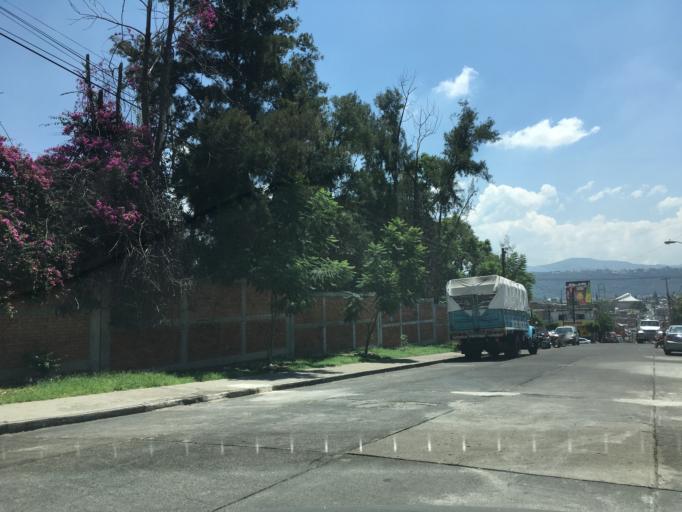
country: MX
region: Michoacan
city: Morelia
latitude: 19.7078
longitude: -101.1732
